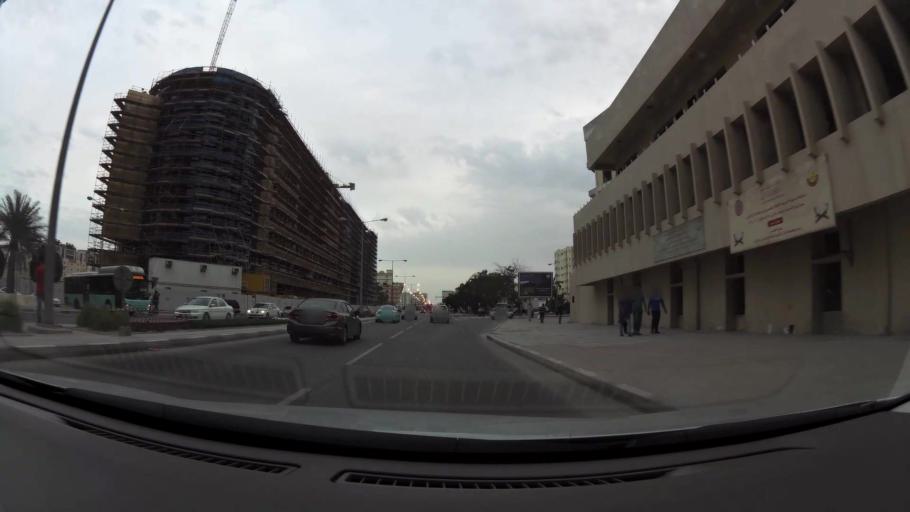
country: QA
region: Baladiyat ad Dawhah
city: Doha
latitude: 25.2726
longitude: 51.5273
